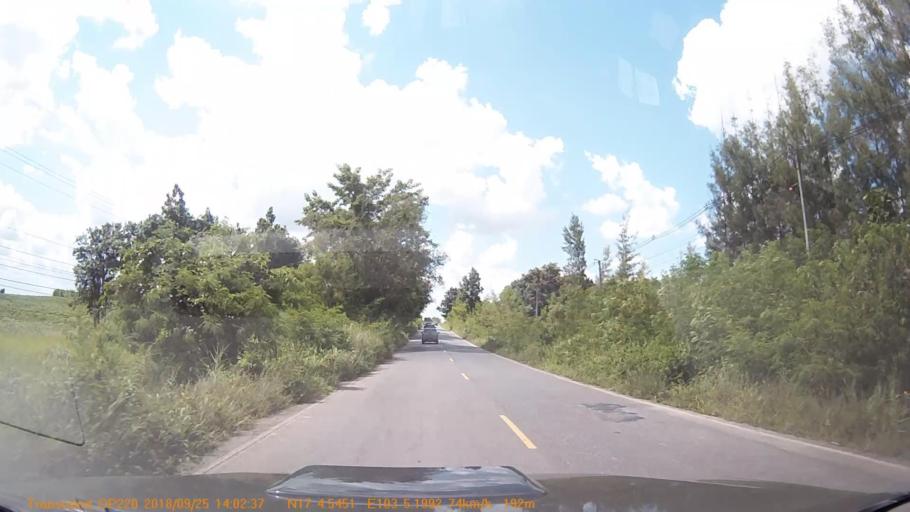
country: TH
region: Changwat Udon Thani
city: Kumphawapi
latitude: 17.0757
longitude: 103.0867
